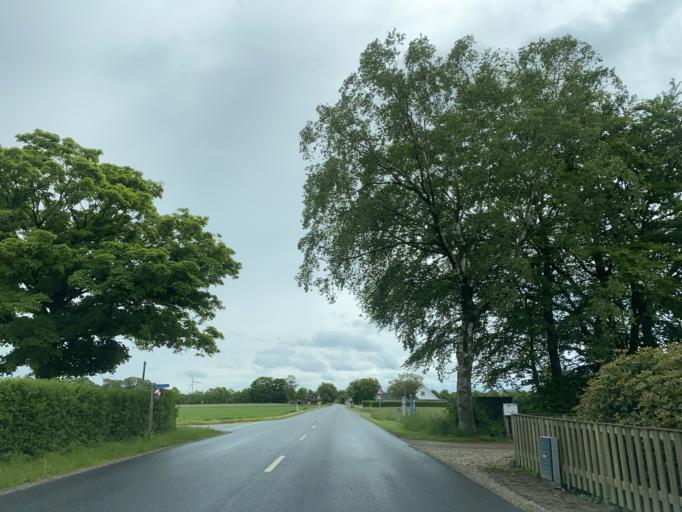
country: DK
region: Central Jutland
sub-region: Arhus Kommune
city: Sabro
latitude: 56.2554
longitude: 9.9636
